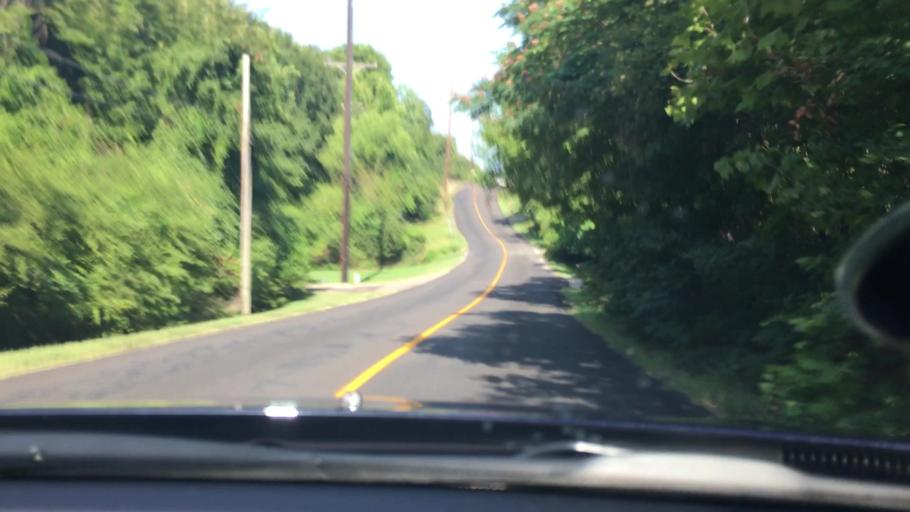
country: US
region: Oklahoma
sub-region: Pontotoc County
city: Ada
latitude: 34.7671
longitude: -96.6494
